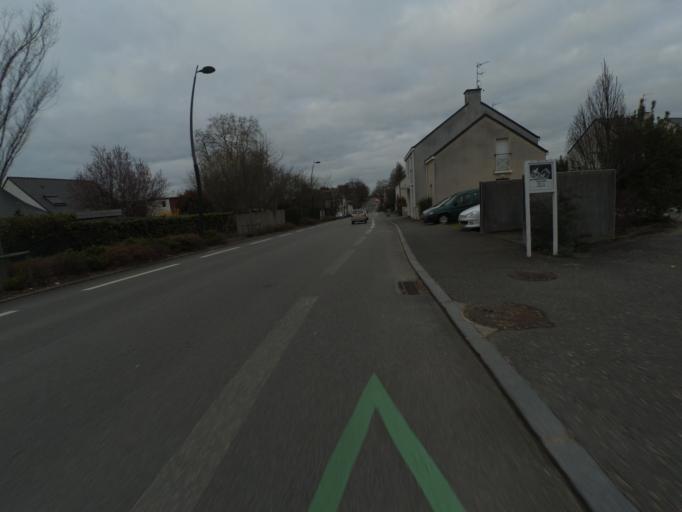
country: FR
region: Pays de la Loire
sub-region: Departement de la Loire-Atlantique
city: Carquefou
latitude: 47.3042
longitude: -1.4849
